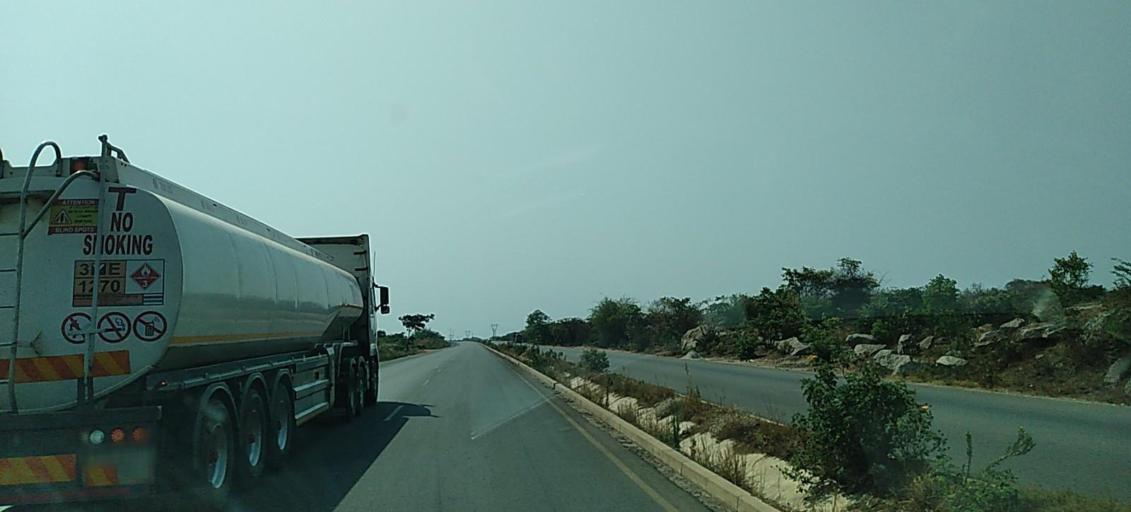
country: ZM
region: Copperbelt
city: Chingola
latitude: -12.5799
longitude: 27.9260
